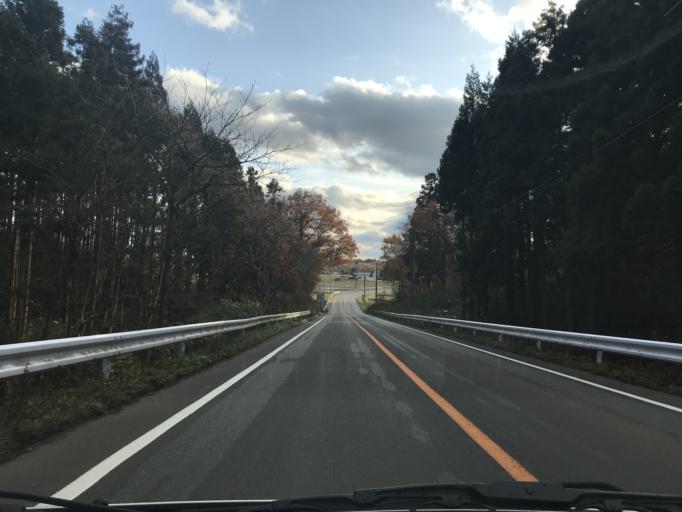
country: JP
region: Iwate
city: Mizusawa
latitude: 39.1563
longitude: 141.0527
